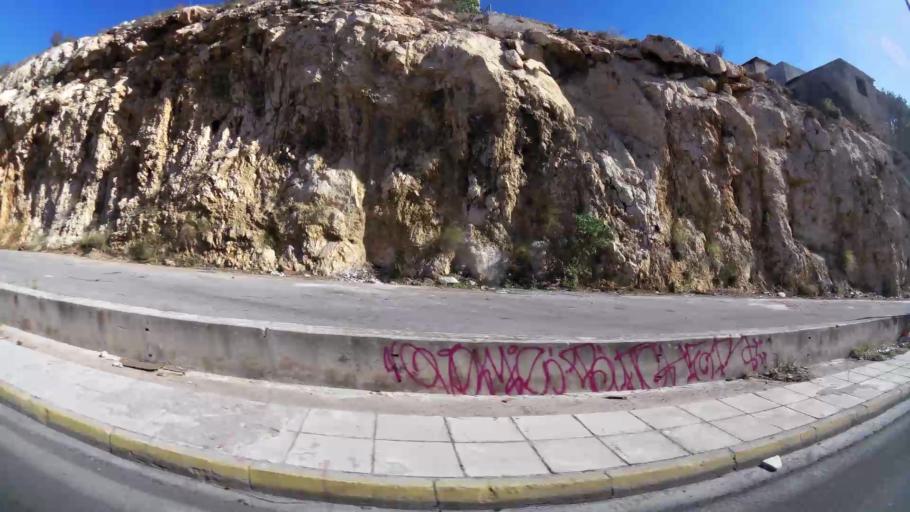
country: GR
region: Attica
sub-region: Nomos Piraios
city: Keratsini
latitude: 37.9683
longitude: 23.6078
